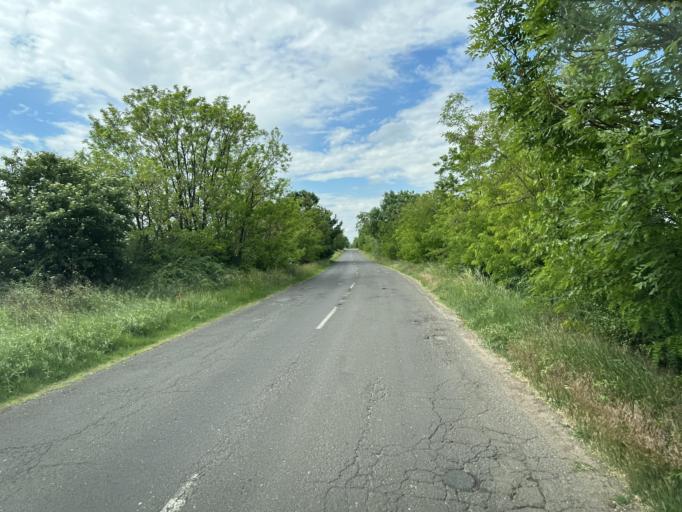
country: HU
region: Pest
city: Szentlorinckata
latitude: 47.5360
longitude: 19.7738
